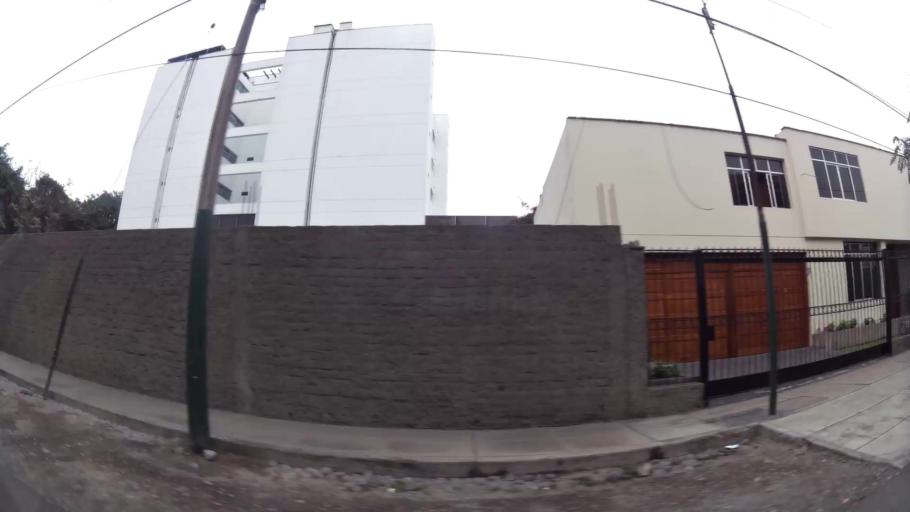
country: PE
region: Lima
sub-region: Lima
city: San Luis
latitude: -12.0920
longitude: -77.0106
